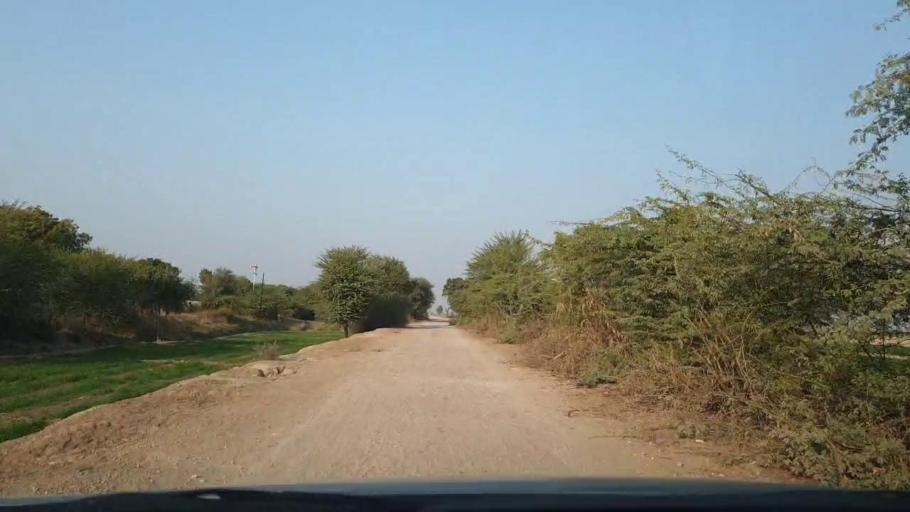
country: PK
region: Sindh
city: Tando Adam
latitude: 25.6950
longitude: 68.6357
